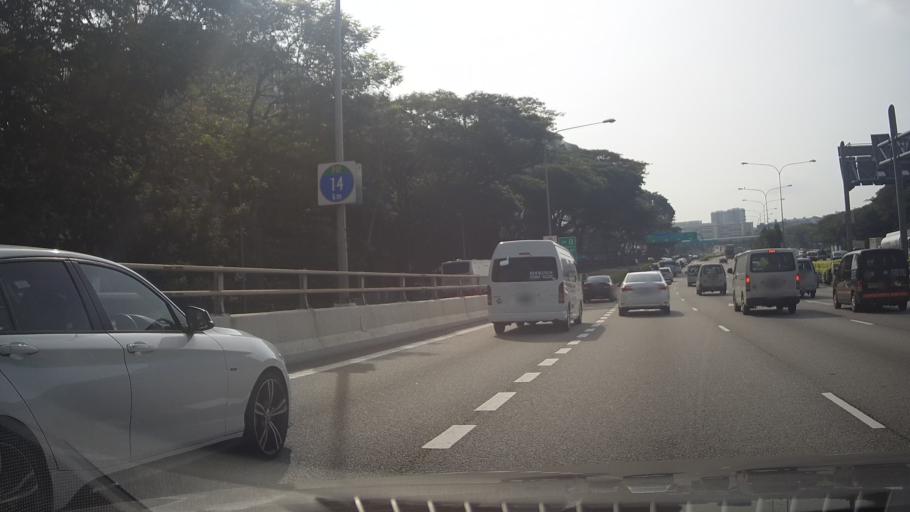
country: SG
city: Singapore
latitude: 1.3268
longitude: 103.8705
